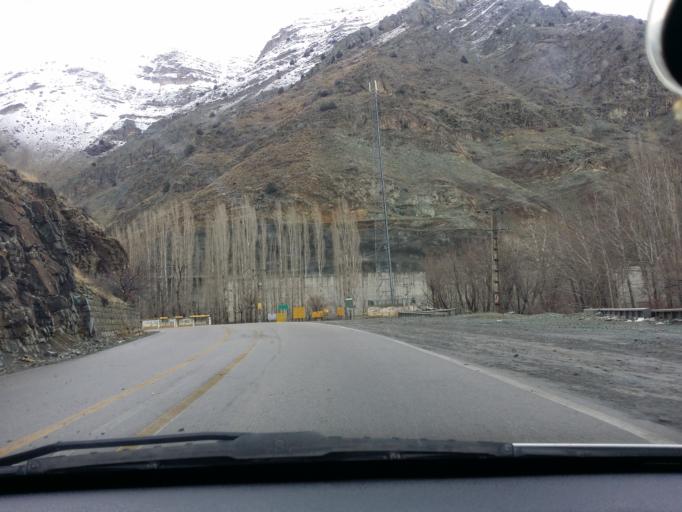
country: IR
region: Tehran
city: Tajrish
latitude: 36.0162
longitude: 51.2976
